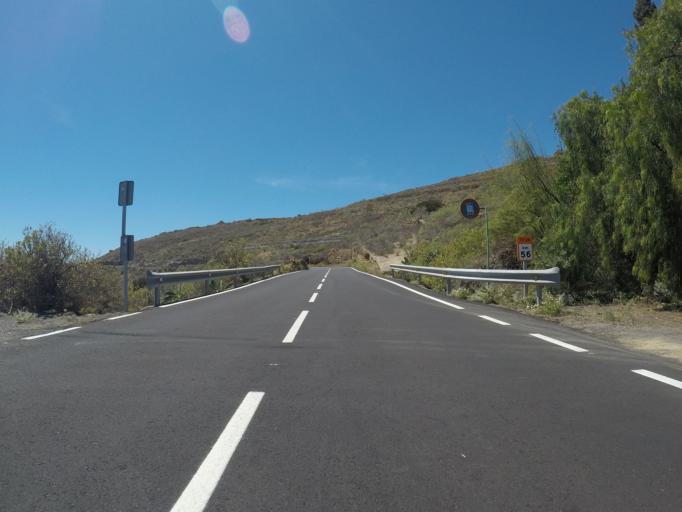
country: ES
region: Canary Islands
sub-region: Provincia de Santa Cruz de Tenerife
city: Lomo de Arico
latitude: 28.1805
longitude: -16.4862
